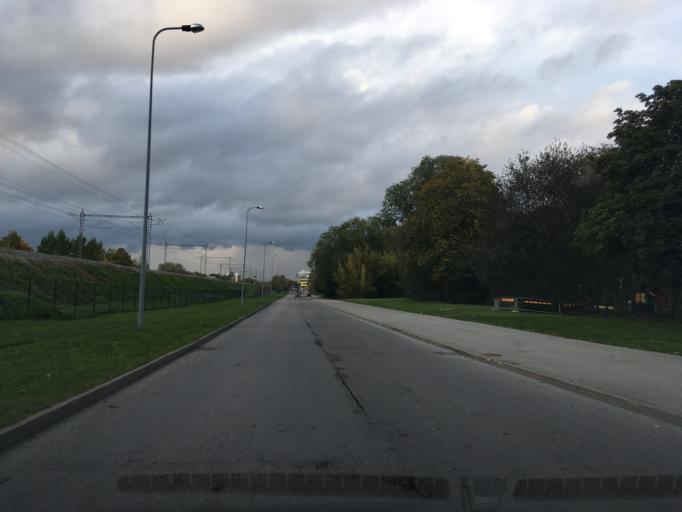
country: EE
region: Harju
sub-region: Tallinna linn
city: Tallinn
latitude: 59.4151
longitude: 24.7339
